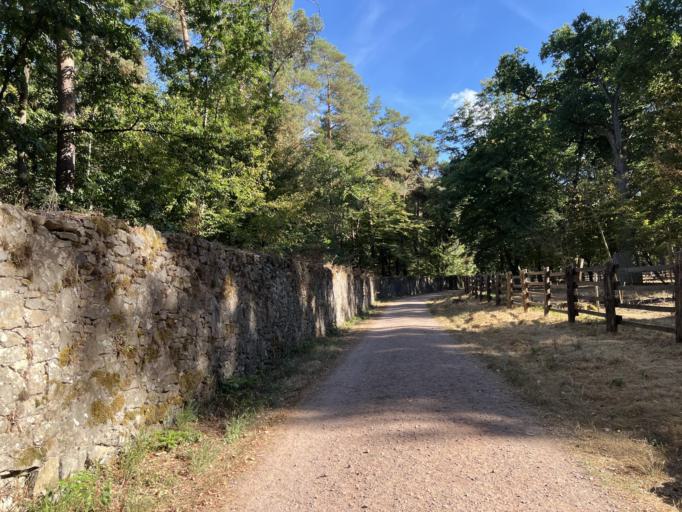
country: DE
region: Hesse
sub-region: Regierungsbezirk Darmstadt
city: Hanau am Main
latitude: 50.0833
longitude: 8.9156
